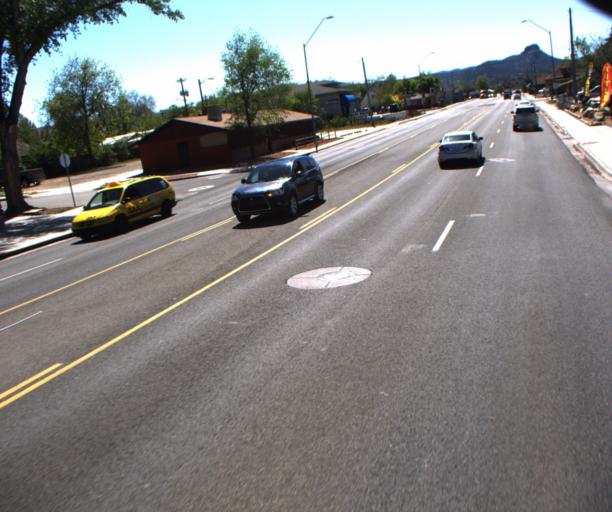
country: US
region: Arizona
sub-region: Yavapai County
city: Prescott
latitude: 34.5454
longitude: -112.4603
